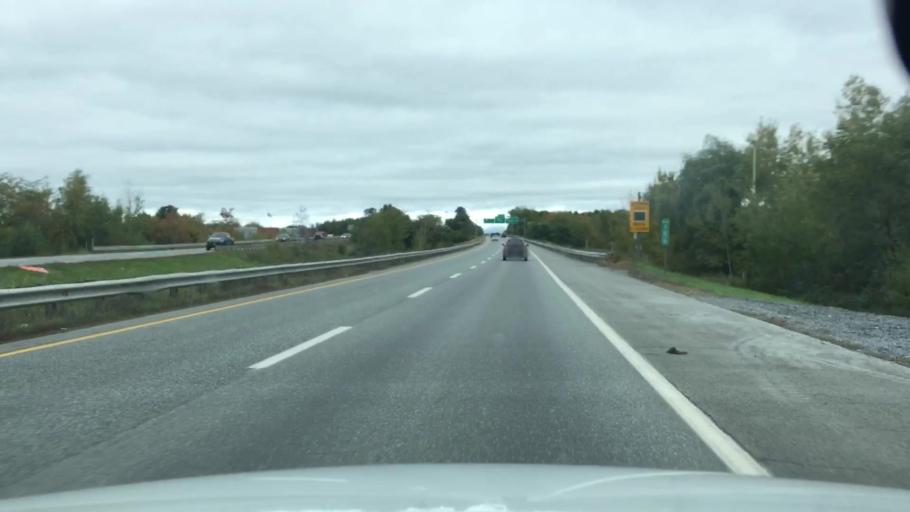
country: US
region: Maine
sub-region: Penobscot County
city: Bangor
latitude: 44.8219
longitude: -68.7645
